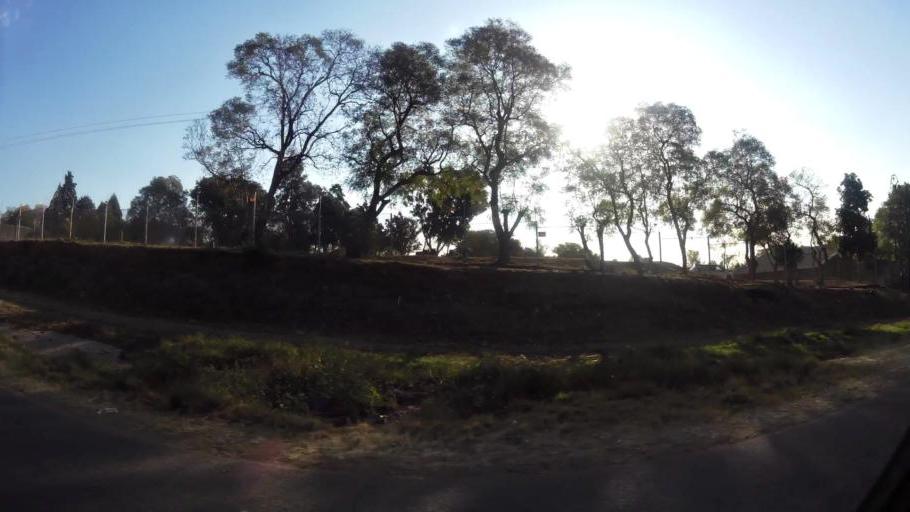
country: ZA
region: Gauteng
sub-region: West Rand District Municipality
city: Muldersdriseloop
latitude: -26.0504
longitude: 27.9057
